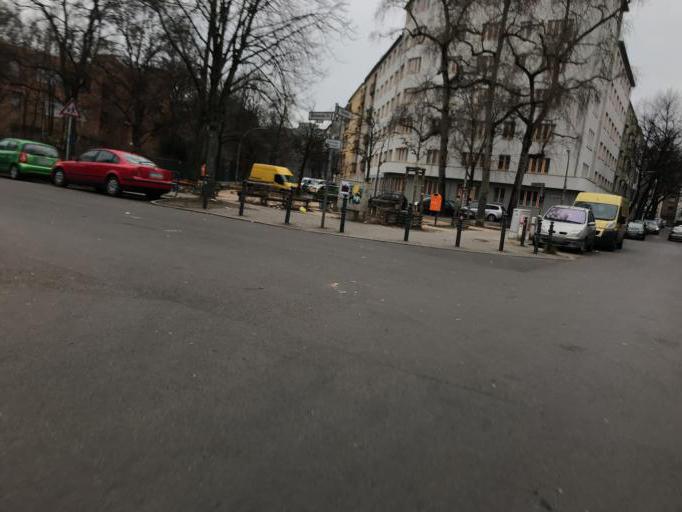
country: DE
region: Berlin
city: Treptow Bezirk
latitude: 52.4725
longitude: 13.4458
